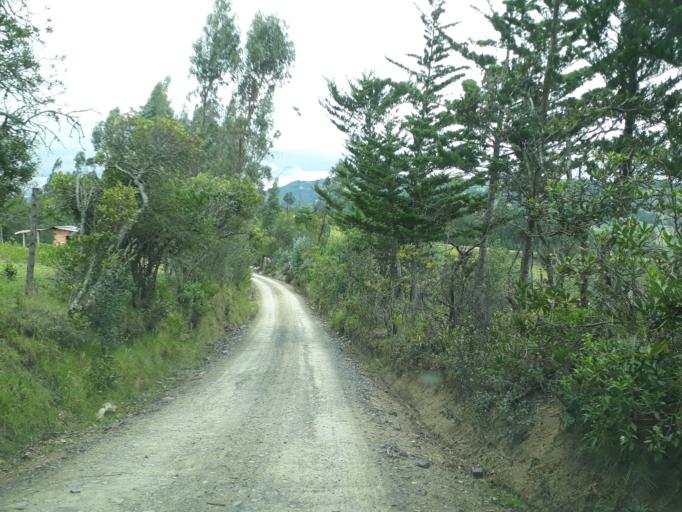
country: CO
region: Boyaca
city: Chiquinquira
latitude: 5.5612
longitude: -73.8134
